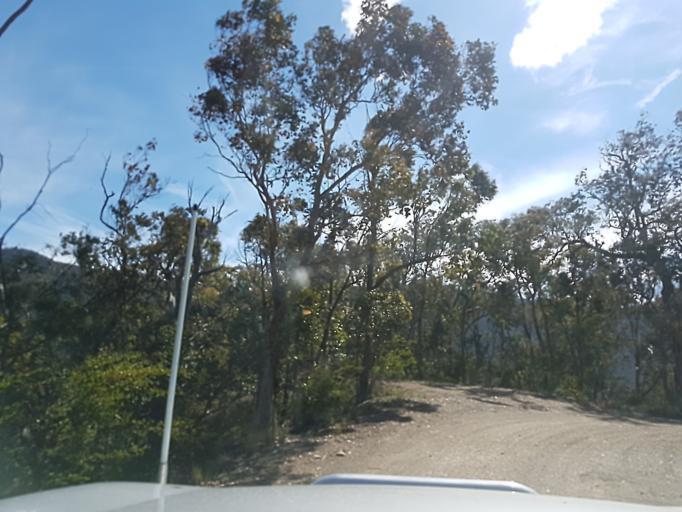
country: AU
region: Victoria
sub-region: Alpine
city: Mount Beauty
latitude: -37.3750
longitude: 147.0420
